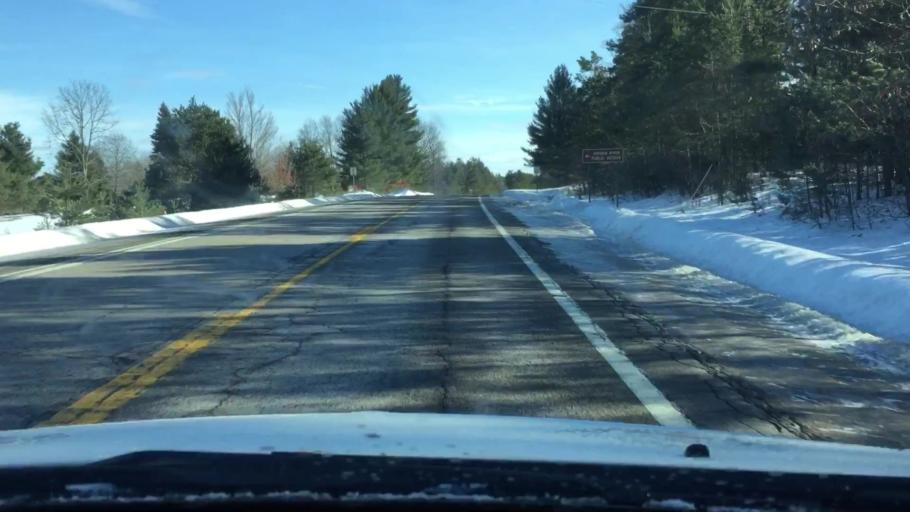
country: US
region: Michigan
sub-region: Charlevoix County
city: East Jordan
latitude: 45.0938
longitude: -85.0990
